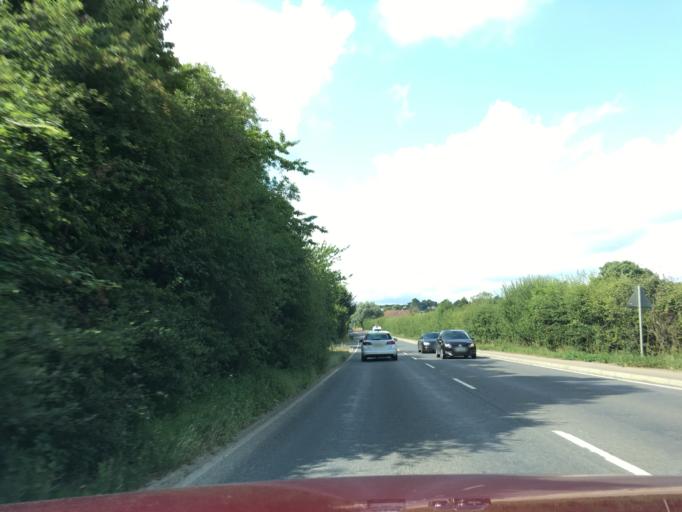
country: GB
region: England
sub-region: Kent
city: Headcorn
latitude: 51.2025
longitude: 0.5936
